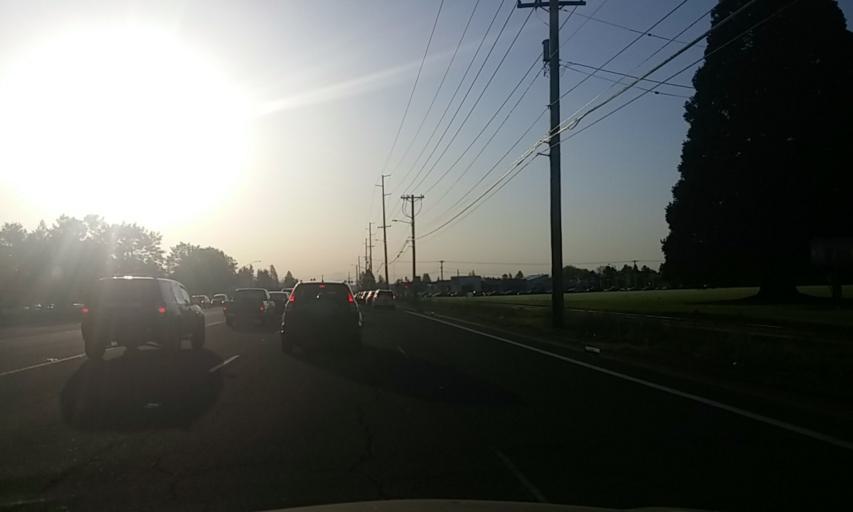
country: US
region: Oregon
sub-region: Washington County
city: Beaverton
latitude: 45.4898
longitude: -122.8292
